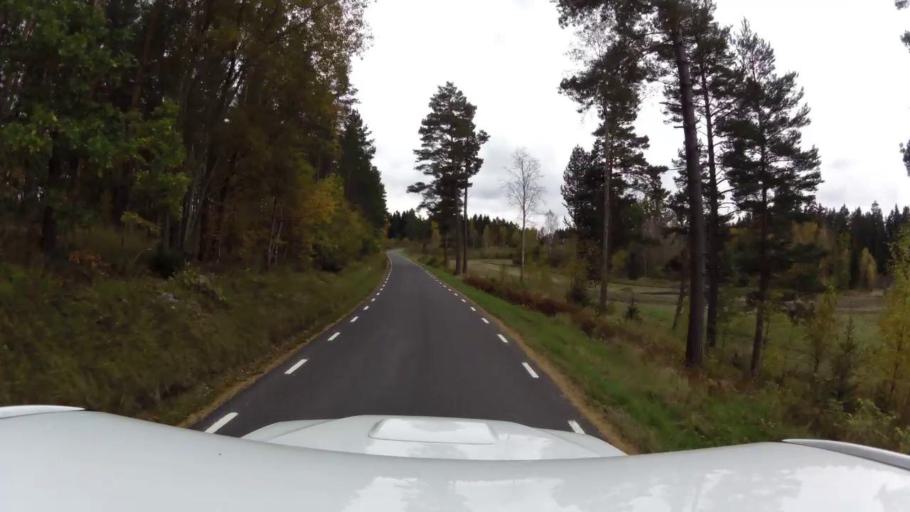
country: SE
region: OEstergoetland
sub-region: Linkopings Kommun
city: Ljungsbro
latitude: 58.5399
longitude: 15.4491
